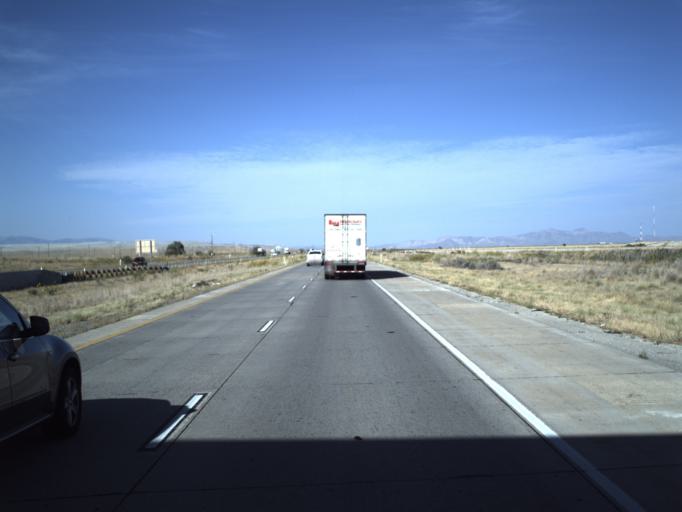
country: US
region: Utah
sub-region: Salt Lake County
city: Magna
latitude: 40.7711
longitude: -112.0632
